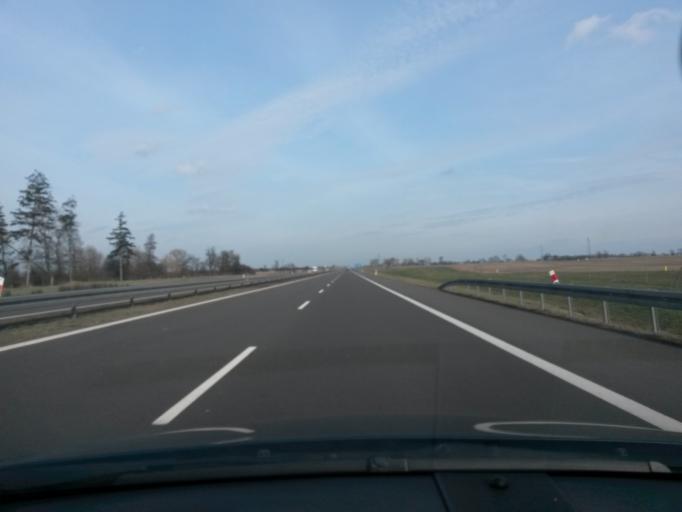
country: PL
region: Greater Poland Voivodeship
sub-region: Powiat wrzesinski
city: Wrzesnia
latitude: 52.3182
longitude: 17.4908
